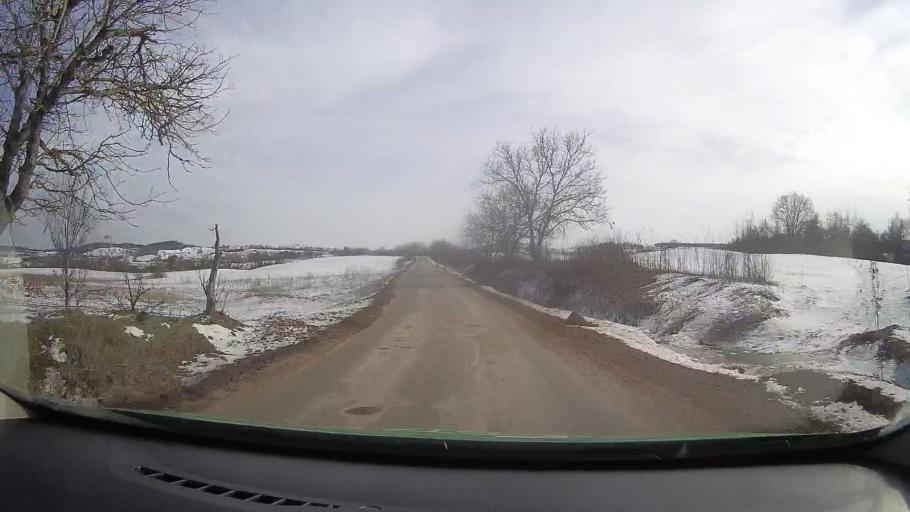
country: RO
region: Mures
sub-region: Comuna Apold
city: Apold
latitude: 46.1169
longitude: 24.8247
